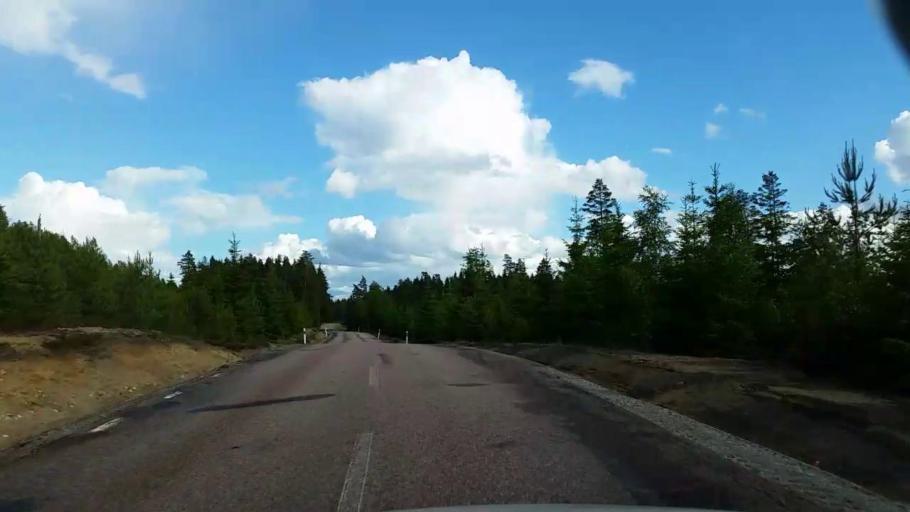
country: SE
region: Vaestmanland
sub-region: Fagersta Kommun
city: Fagersta
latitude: 59.8892
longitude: 15.8259
